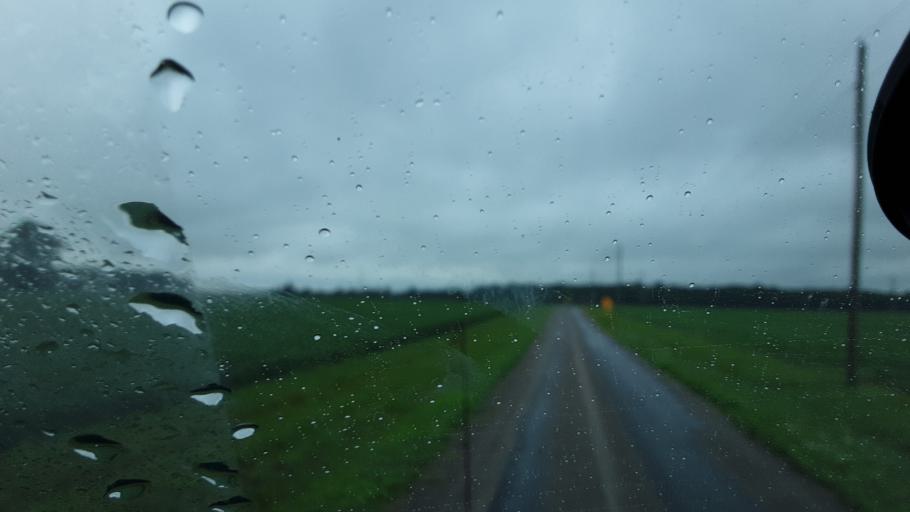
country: US
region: Ohio
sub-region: Mercer County
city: Rockford
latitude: 40.7547
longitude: -84.6526
